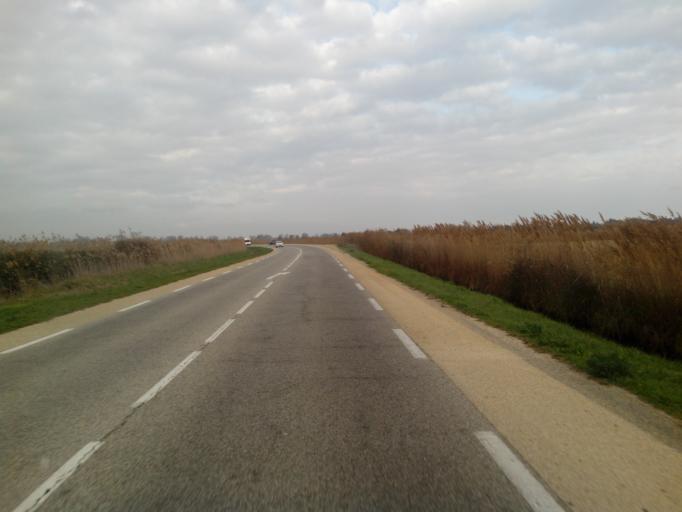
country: FR
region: Languedoc-Roussillon
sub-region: Departement du Gard
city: Saint-Gilles
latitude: 43.5661
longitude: 4.4204
